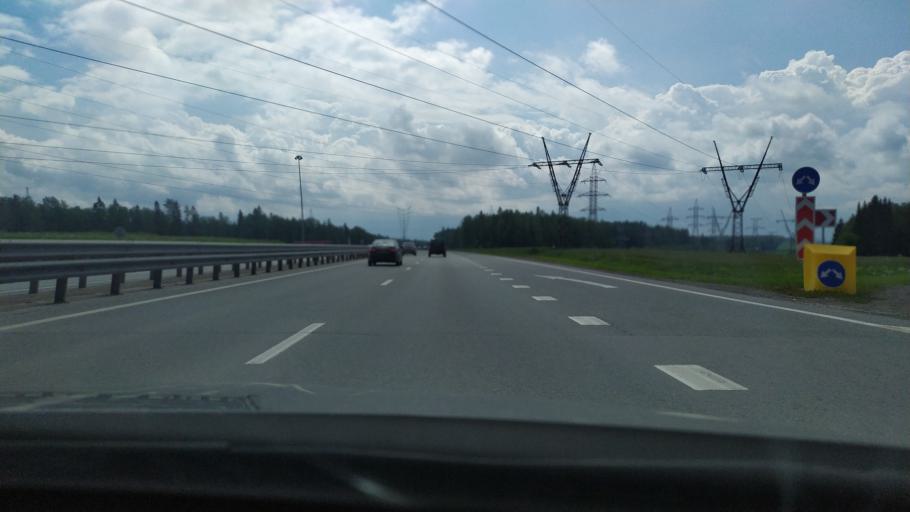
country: RU
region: Perm
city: Novyye Lyady
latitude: 58.0444
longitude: 56.4305
